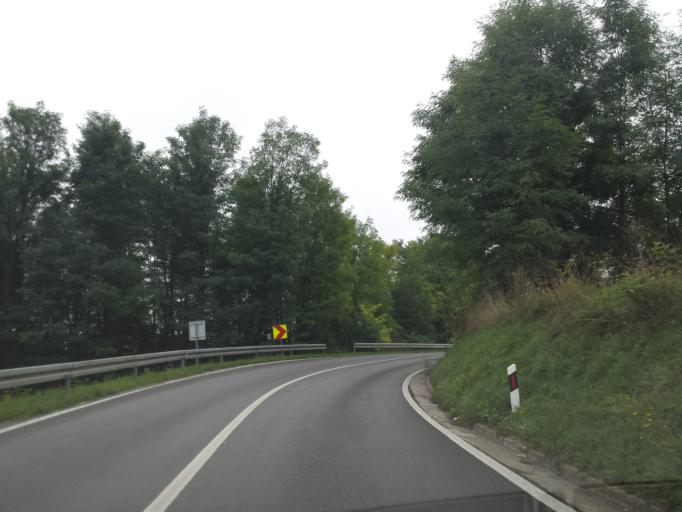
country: HR
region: Karlovacka
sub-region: Grad Karlovac
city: Karlovac
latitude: 45.4106
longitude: 15.4514
